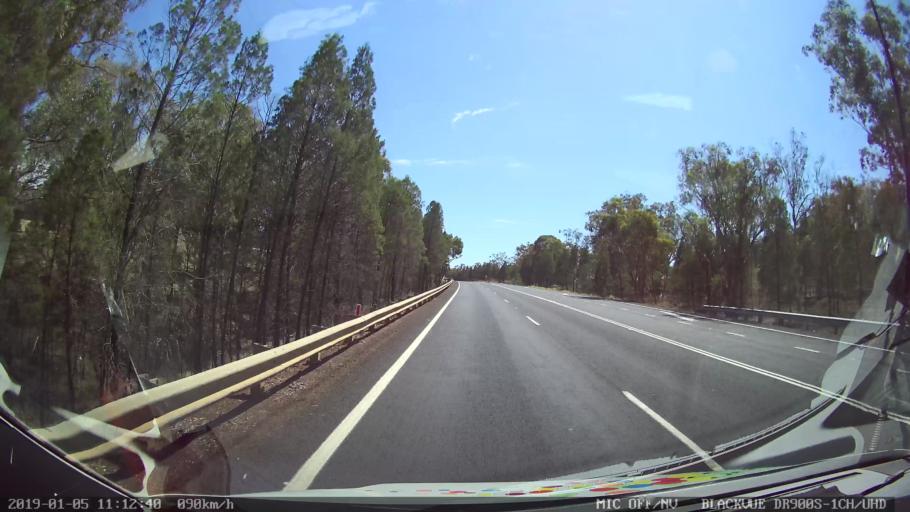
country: AU
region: New South Wales
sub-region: Warrumbungle Shire
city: Coonabarabran
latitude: -31.3797
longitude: 149.2633
